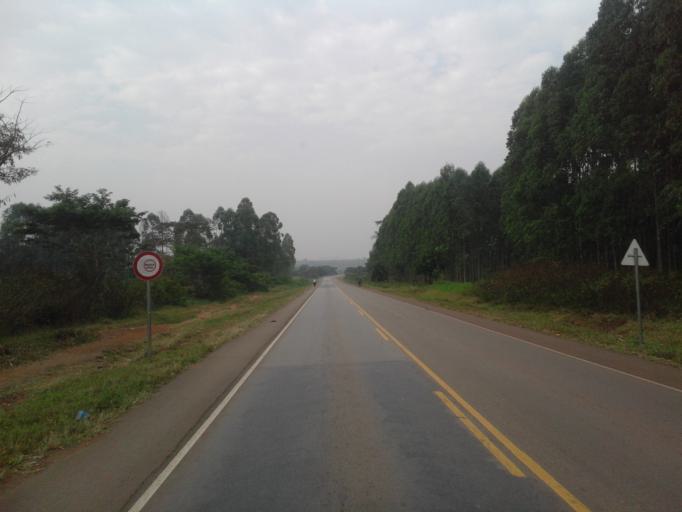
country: UG
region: Eastern Region
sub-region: Busia District
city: Busia
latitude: 0.5960
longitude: 34.0617
